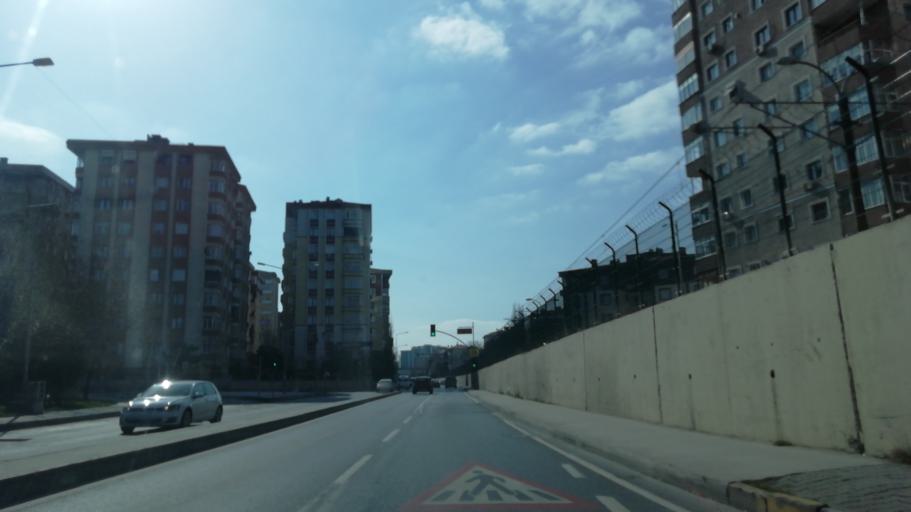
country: TR
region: Istanbul
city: merter keresteciler
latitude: 41.0179
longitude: 28.9008
